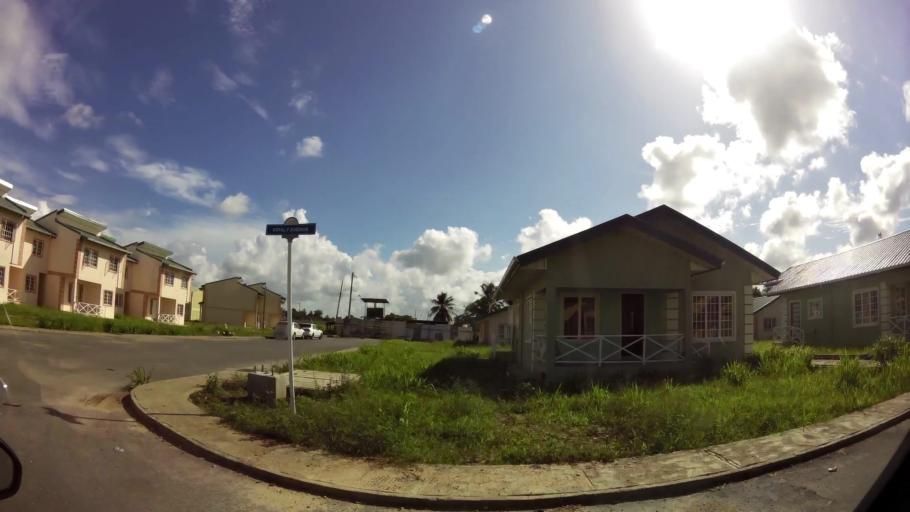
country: TT
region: Chaguanas
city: Chaguanas
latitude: 10.5336
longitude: -61.3922
